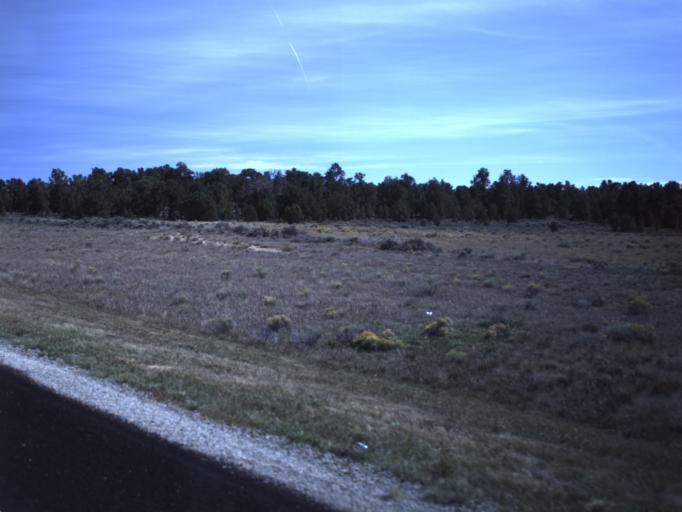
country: US
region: Colorado
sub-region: Dolores County
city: Dove Creek
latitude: 37.8323
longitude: -109.0972
